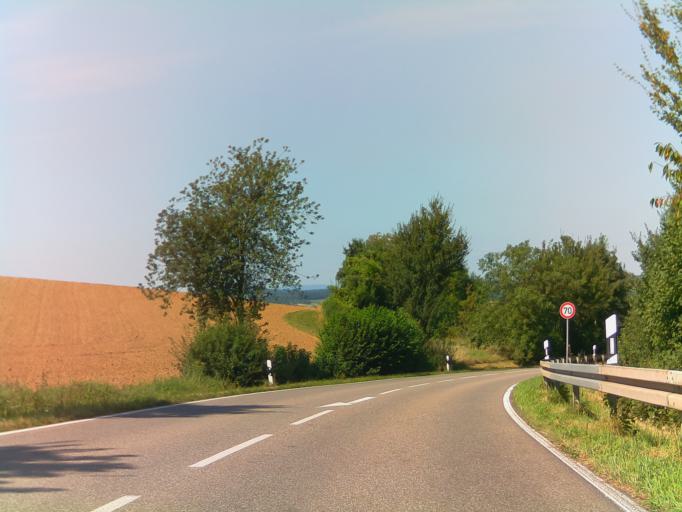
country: DE
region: Baden-Wuerttemberg
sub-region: Karlsruhe Region
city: Bretten
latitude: 49.1009
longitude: 8.7144
